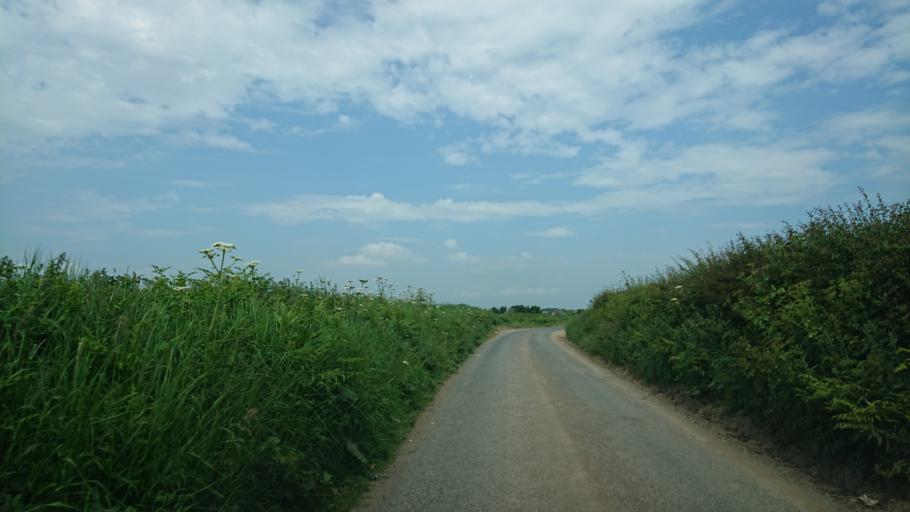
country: IE
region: Munster
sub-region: Waterford
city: Dunmore East
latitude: 52.2087
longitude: -6.9916
